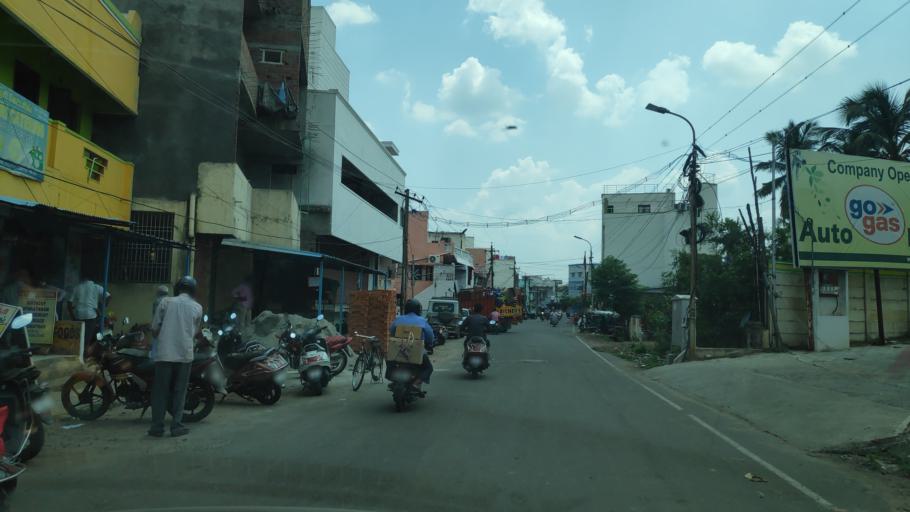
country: IN
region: Tamil Nadu
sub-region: Thiruvallur
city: Ambattur
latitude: 13.1175
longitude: 80.1566
